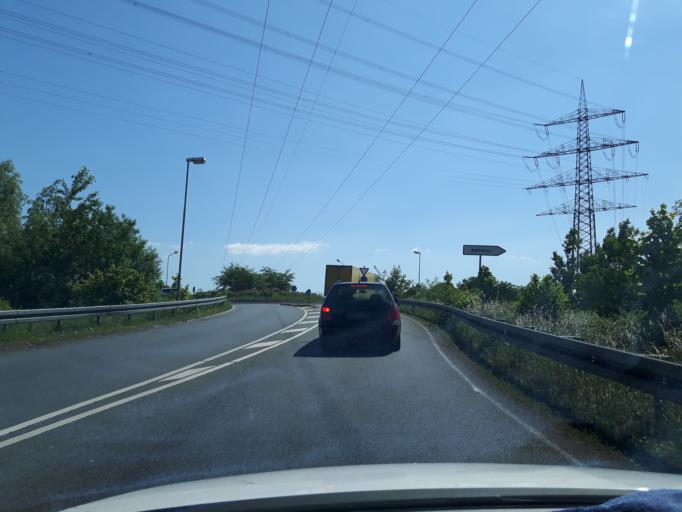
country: DE
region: North Rhine-Westphalia
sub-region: Regierungsbezirk Dusseldorf
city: Ratingen
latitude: 51.3446
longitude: 6.8233
